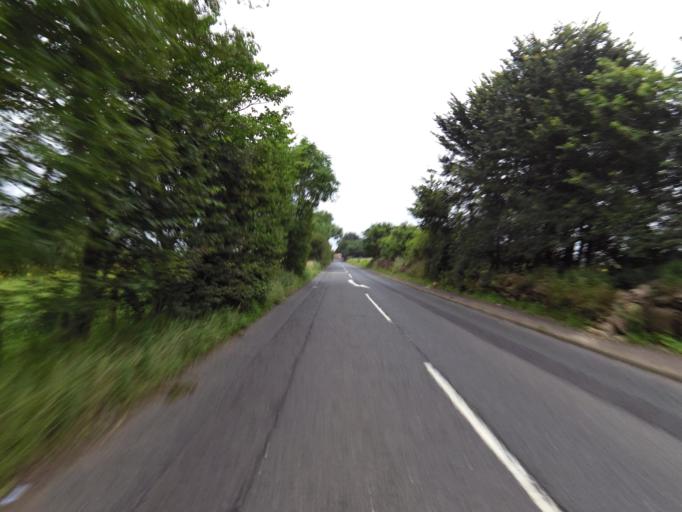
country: GB
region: Scotland
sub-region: Midlothian
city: Dalkeith
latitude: 55.9199
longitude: -3.0711
